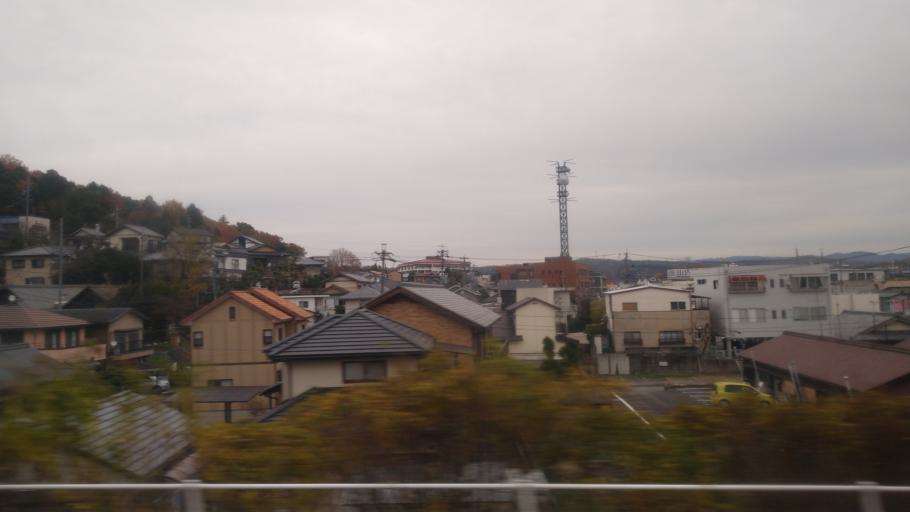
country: JP
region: Gifu
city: Tajimi
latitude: 35.3418
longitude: 137.1275
